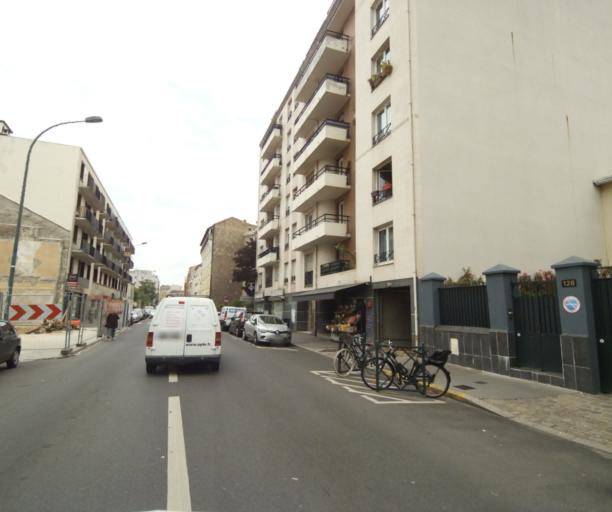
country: FR
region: Ile-de-France
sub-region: Departement des Hauts-de-Seine
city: Asnieres-sur-Seine
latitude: 48.9162
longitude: 2.2824
